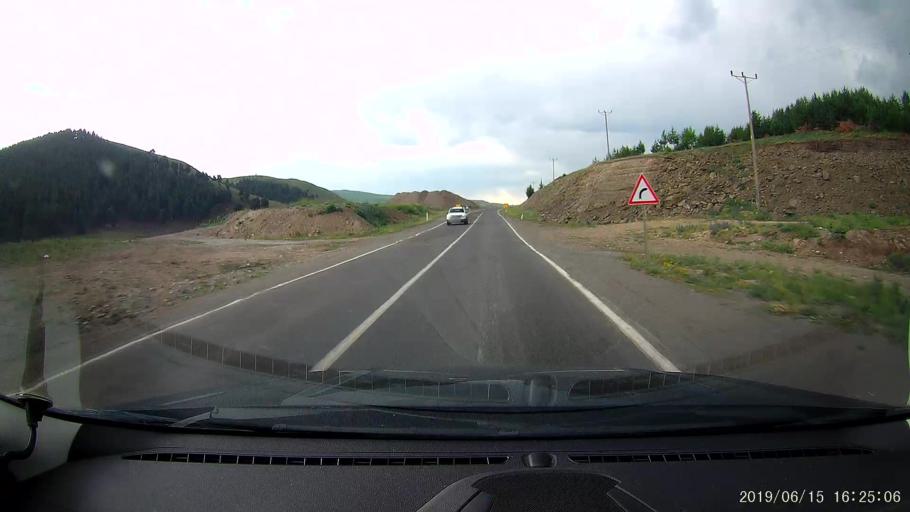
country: TR
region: Ardahan
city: Hanak
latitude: 41.1580
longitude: 42.8715
